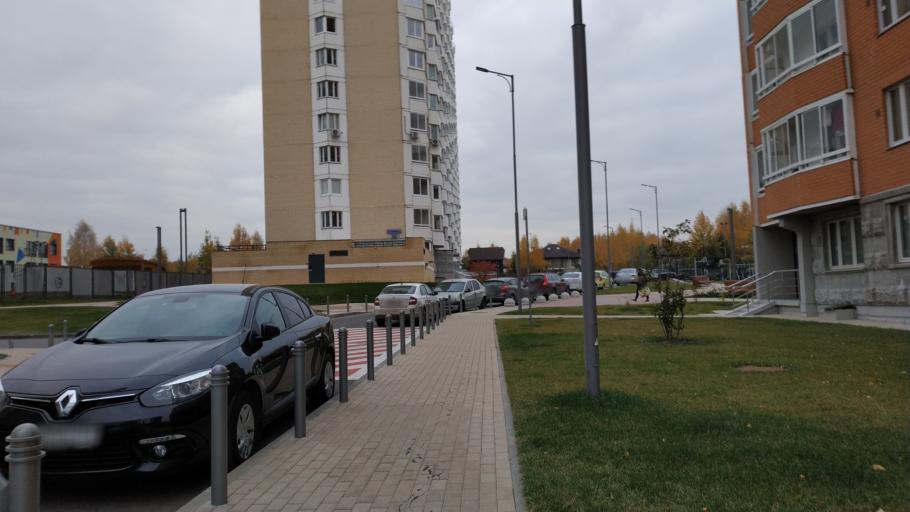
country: RU
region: Moscow
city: Novo-Peredelkino
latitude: 55.6365
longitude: 37.3164
